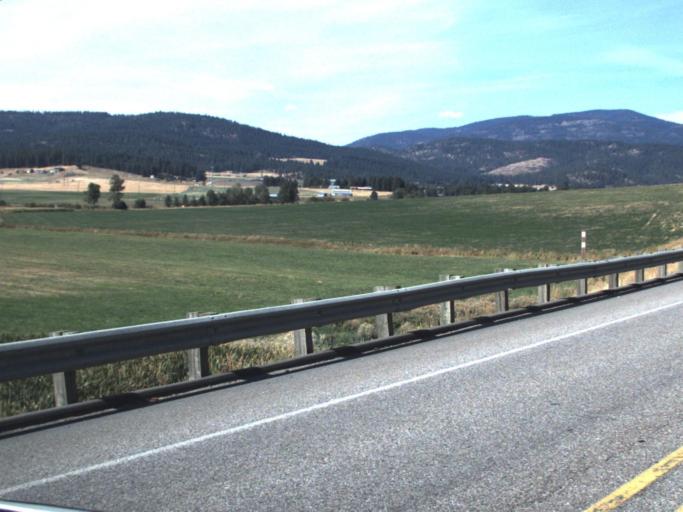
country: US
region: Washington
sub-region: Stevens County
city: Chewelah
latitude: 48.3069
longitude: -117.7791
